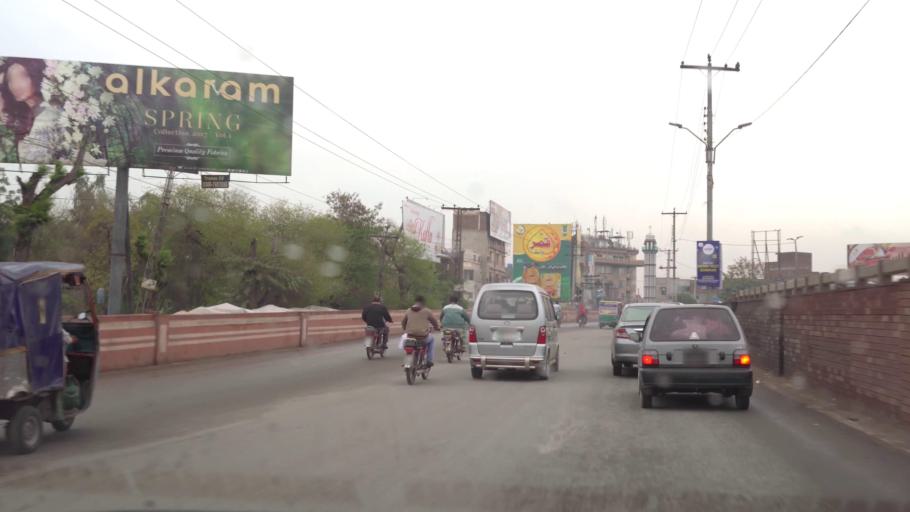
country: PK
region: Punjab
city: Faisalabad
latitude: 31.4206
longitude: 73.0967
